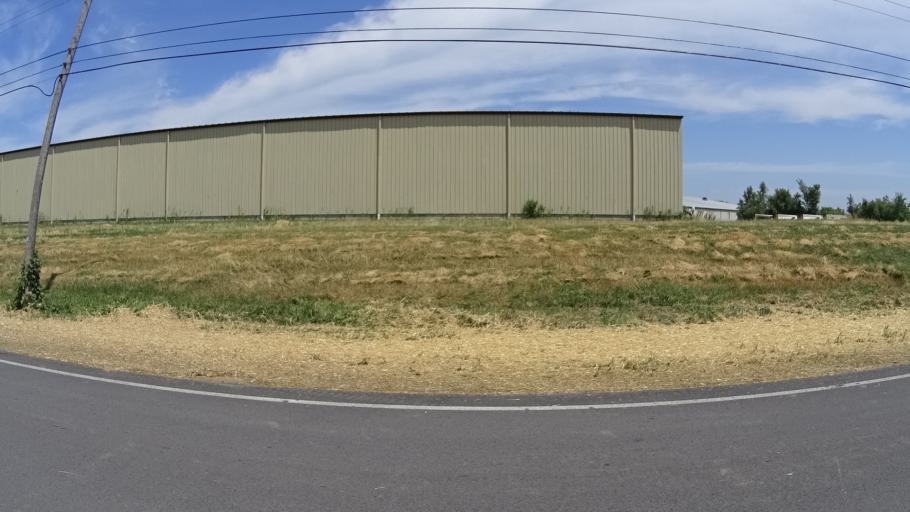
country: US
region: Ohio
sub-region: Erie County
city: Sandusky
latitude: 41.4115
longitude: -82.7716
